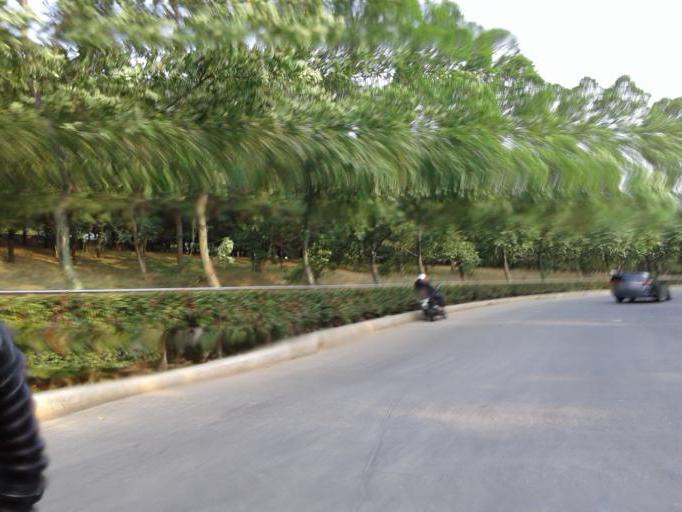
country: ID
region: Banten
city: South Tangerang
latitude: -6.2840
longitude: 106.7300
